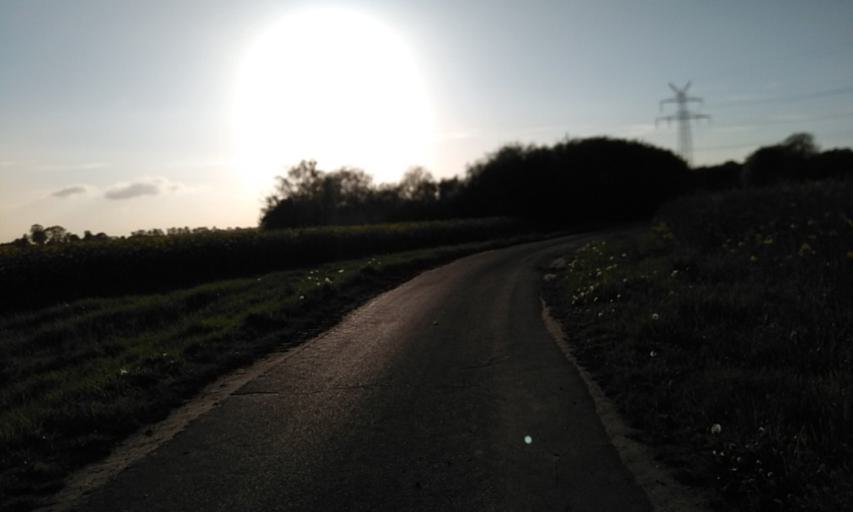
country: DE
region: Lower Saxony
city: Harsefeld
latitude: 53.4082
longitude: 9.5065
